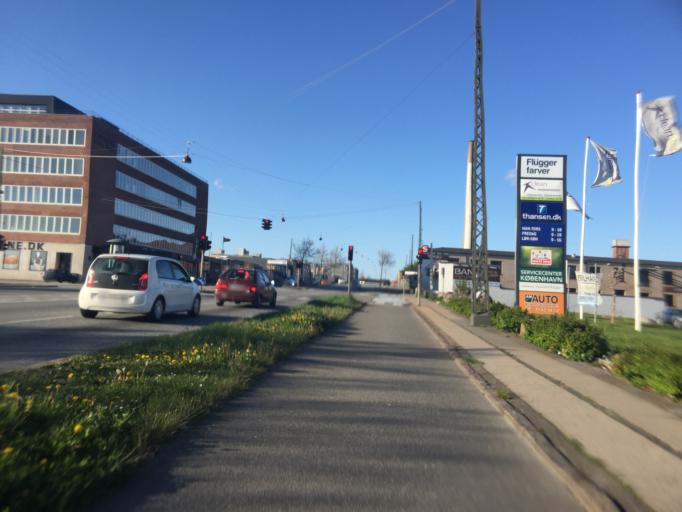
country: DK
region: Capital Region
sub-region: Frederiksberg Kommune
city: Frederiksberg
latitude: 55.6529
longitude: 12.5099
